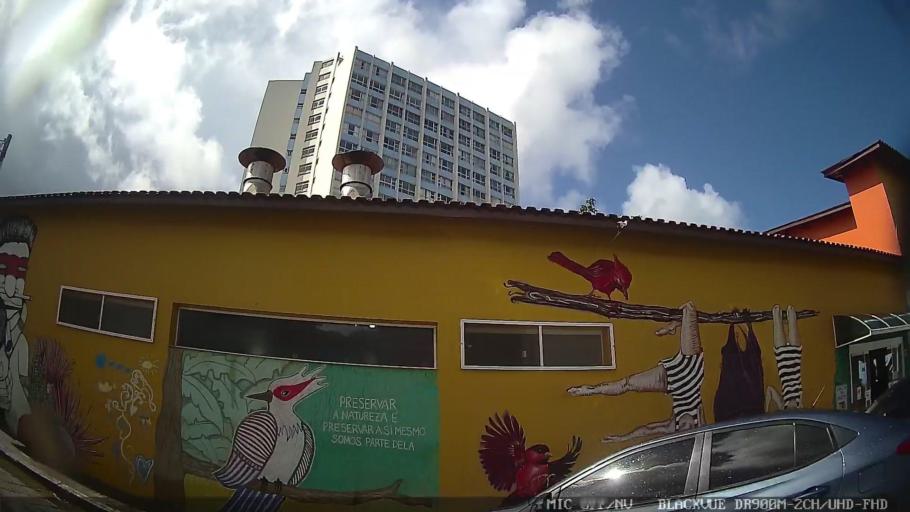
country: BR
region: Sao Paulo
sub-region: Itanhaem
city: Itanhaem
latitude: -24.1894
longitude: -46.8020
